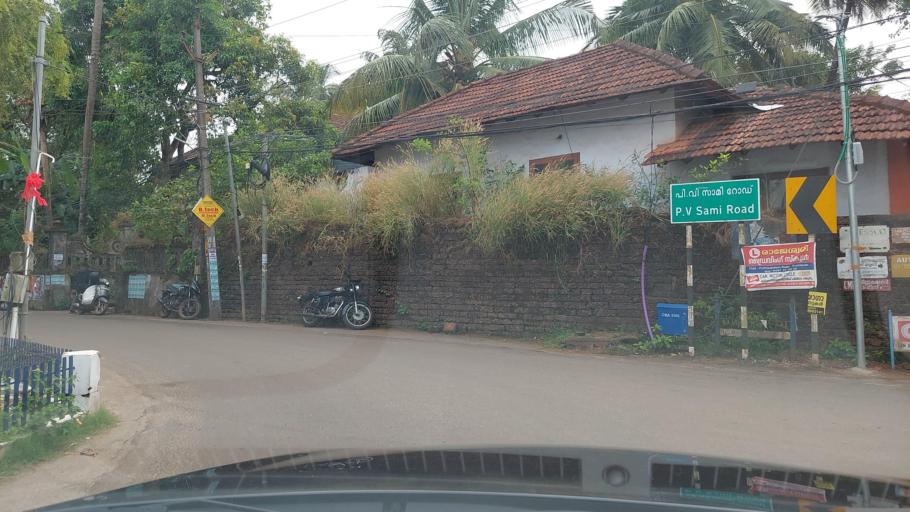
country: IN
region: Kerala
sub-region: Kozhikode
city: Kozhikode
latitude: 11.2455
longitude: 75.7873
